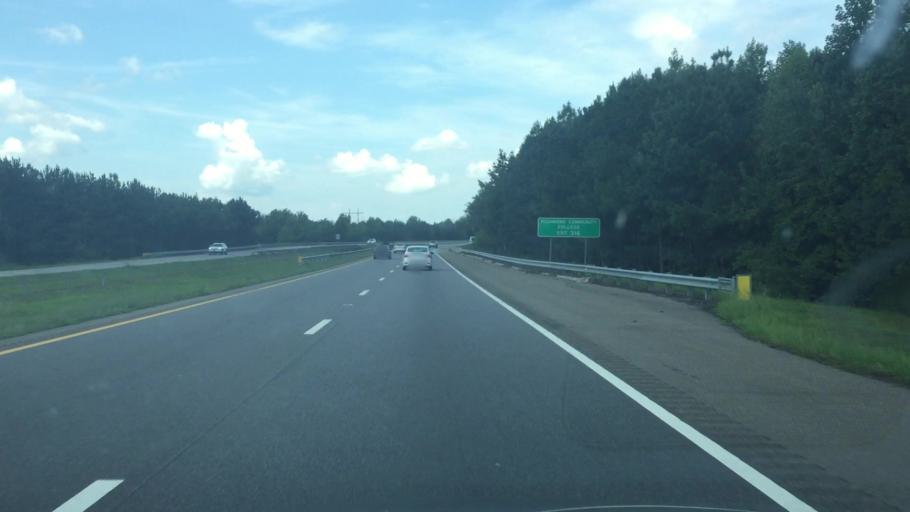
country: US
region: North Carolina
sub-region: Richmond County
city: Hamlet
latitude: 34.8527
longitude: -79.7272
